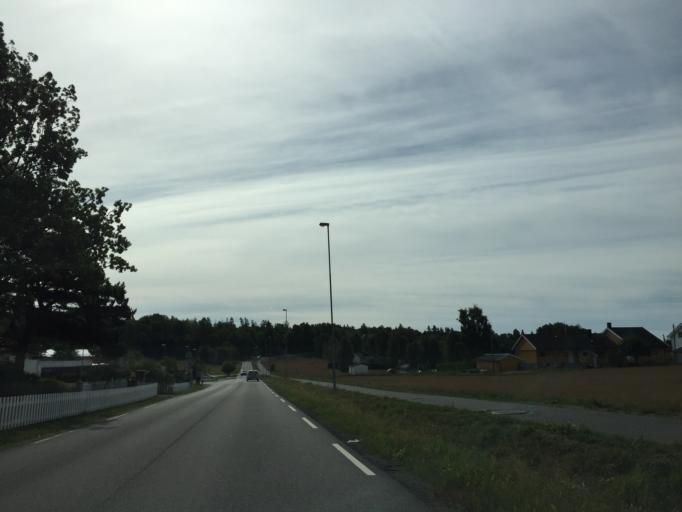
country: NO
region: Ostfold
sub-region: Moss
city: Moss
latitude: 59.4950
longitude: 10.6887
